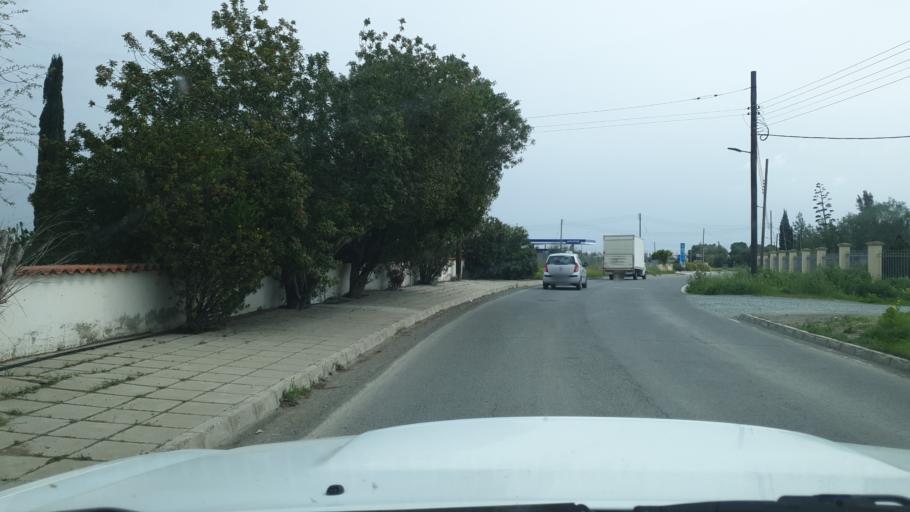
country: CY
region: Lefkosia
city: Tseri
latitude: 35.1060
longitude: 33.3630
